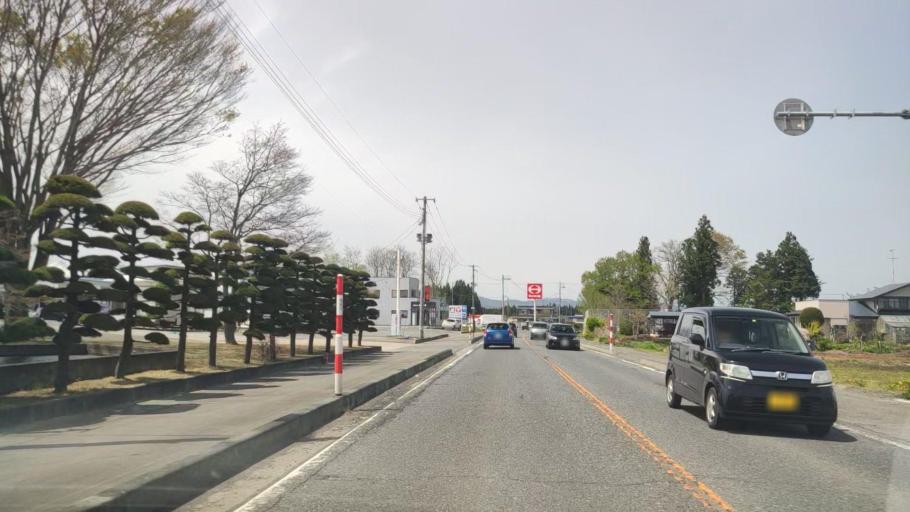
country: JP
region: Aomori
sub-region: Misawa Shi
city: Inuotose
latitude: 40.6736
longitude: 141.1789
